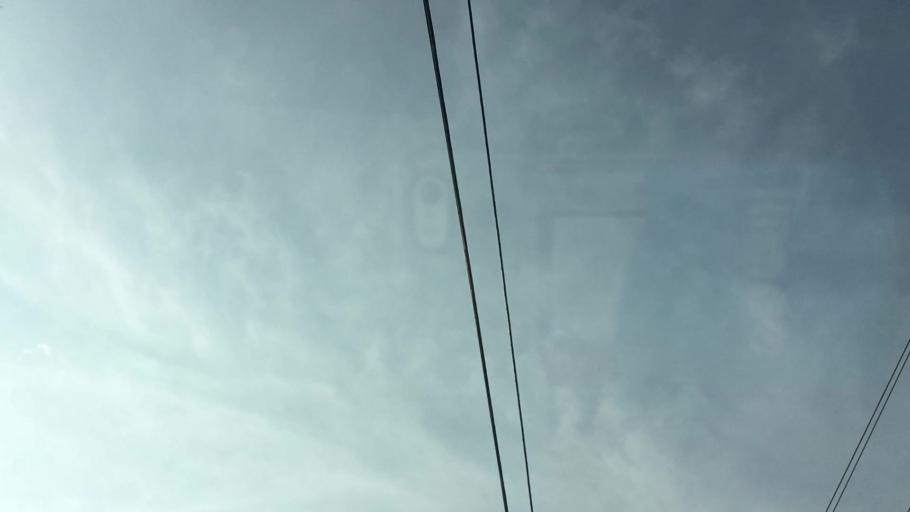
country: US
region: Alabama
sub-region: Bibb County
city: Woodstock
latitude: 33.2154
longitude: -87.1020
